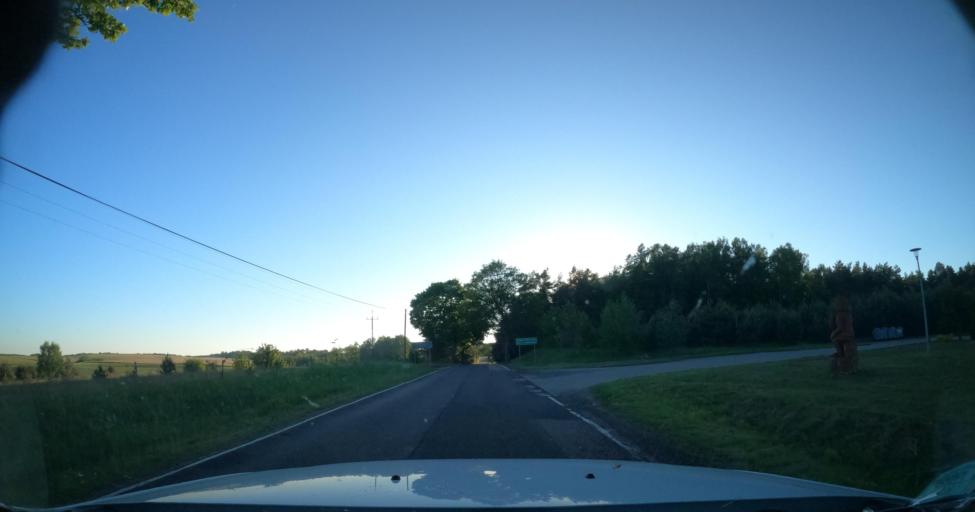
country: PL
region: Pomeranian Voivodeship
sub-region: Powiat bytowski
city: Czarna Dabrowka
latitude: 54.3584
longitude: 17.5495
